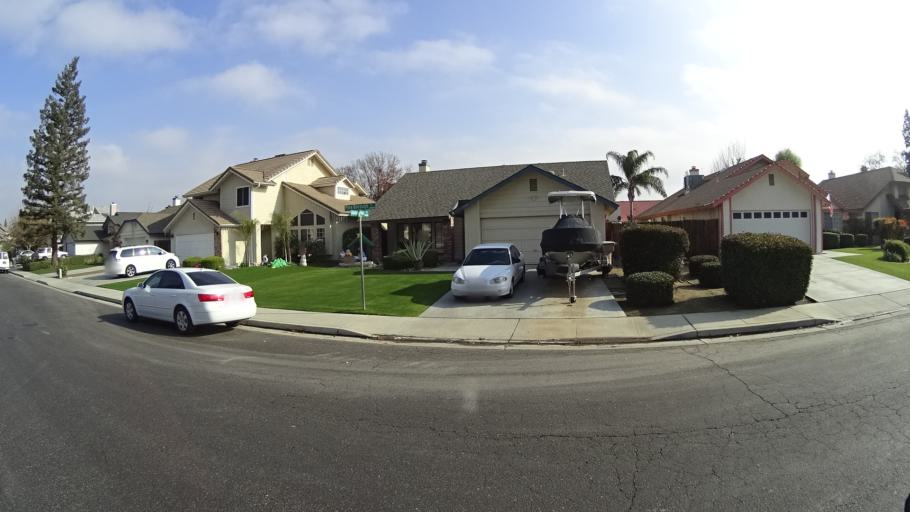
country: US
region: California
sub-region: Kern County
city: Greenfield
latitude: 35.2976
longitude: -119.0861
